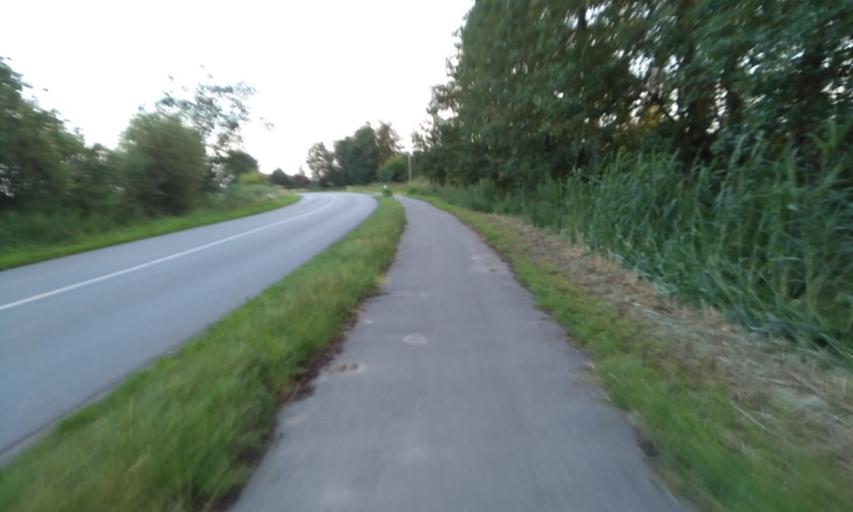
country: DE
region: Lower Saxony
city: Jork
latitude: 53.5136
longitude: 9.7197
